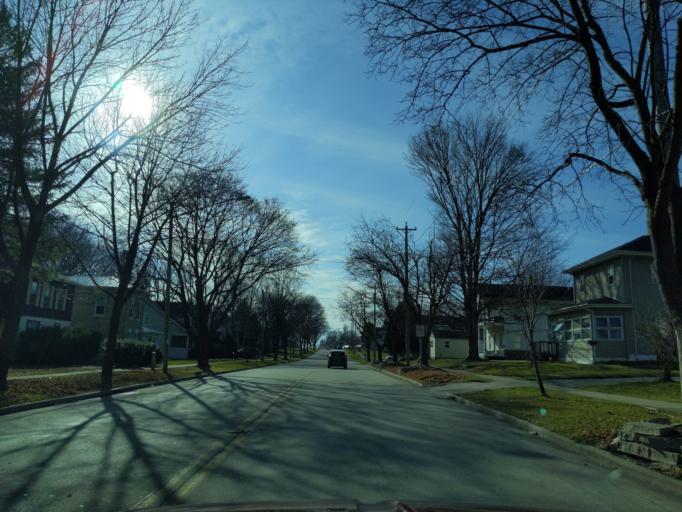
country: US
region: Wisconsin
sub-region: Walworth County
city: Whitewater
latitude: 42.8297
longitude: -88.7404
